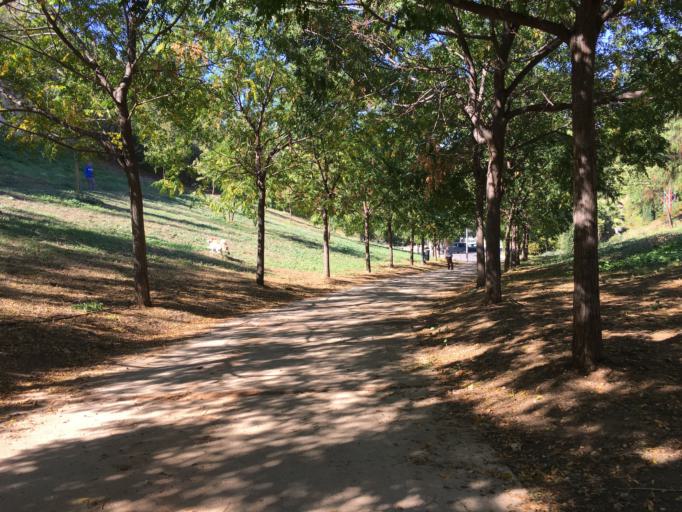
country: ES
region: Andalusia
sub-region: Provincia de Granada
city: Granada
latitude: 37.1847
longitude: -3.5955
